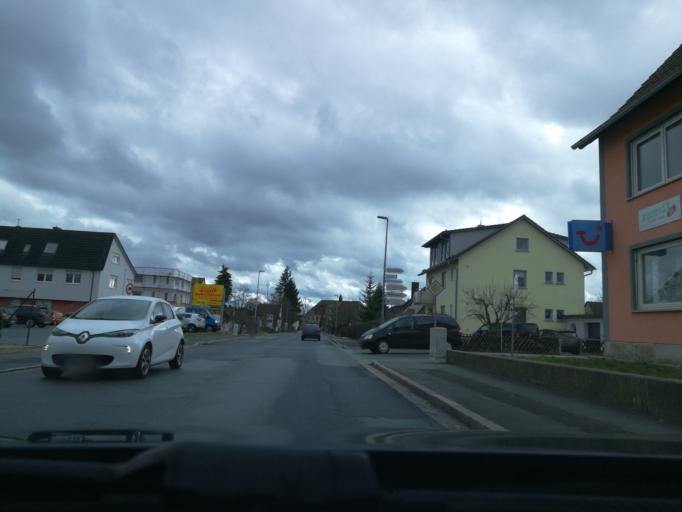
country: DE
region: Bavaria
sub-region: Regierungsbezirk Mittelfranken
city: Hemhofen
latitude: 49.6863
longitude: 10.9386
